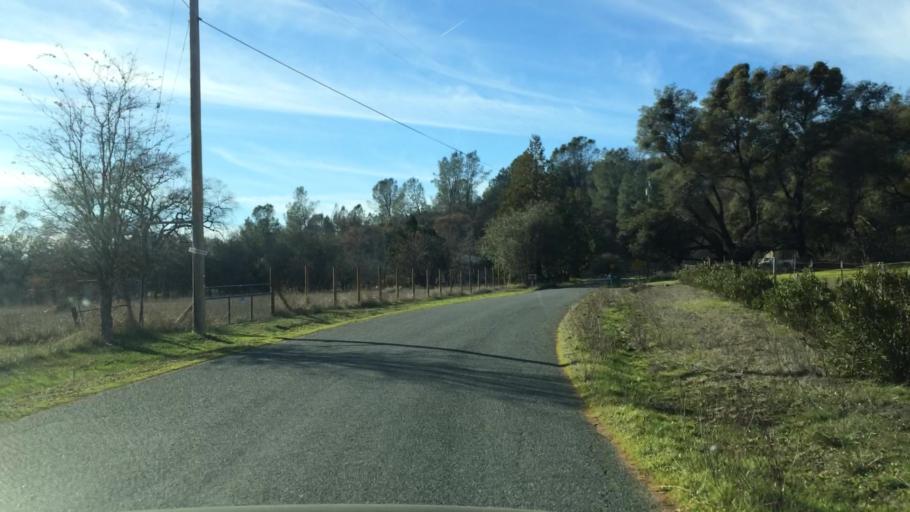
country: US
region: California
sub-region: Nevada County
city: Penn Valley
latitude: 39.2114
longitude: -121.1704
